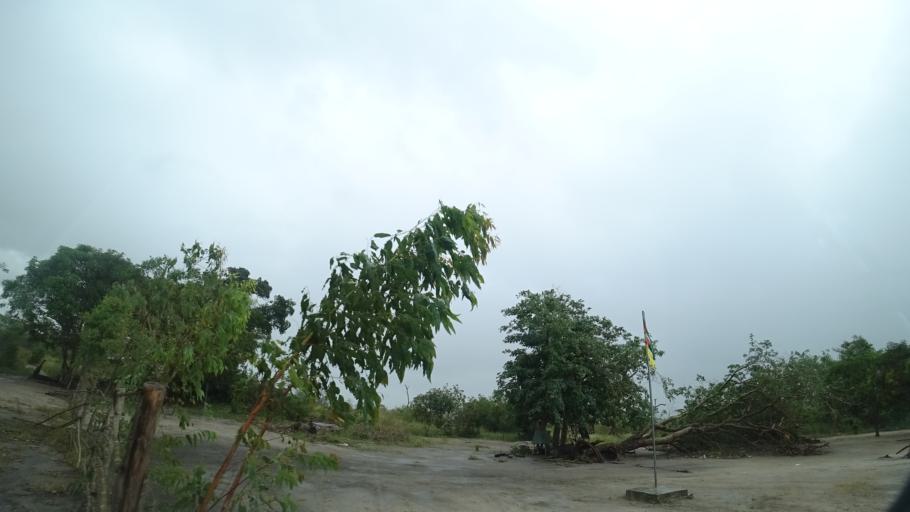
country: MZ
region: Sofala
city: Dondo
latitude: -19.5501
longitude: 35.0529
